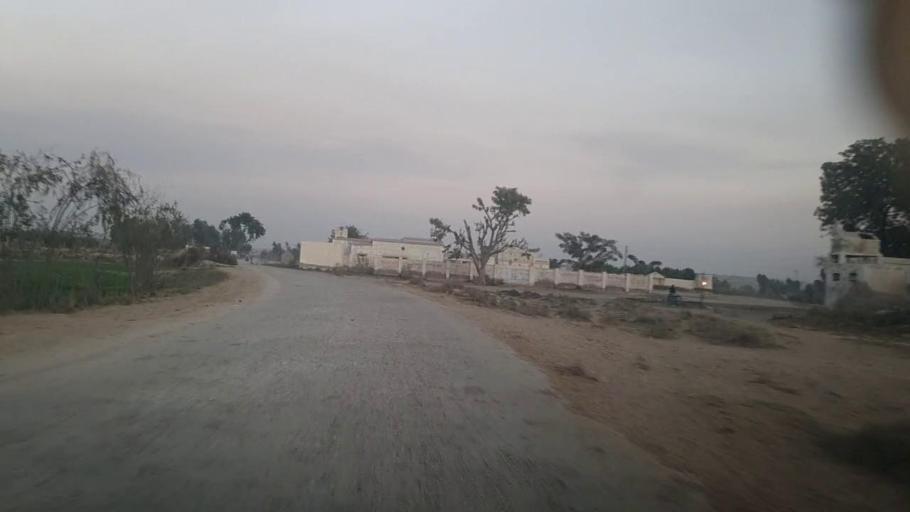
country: PK
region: Sindh
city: Kandiari
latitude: 26.6765
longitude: 68.9523
